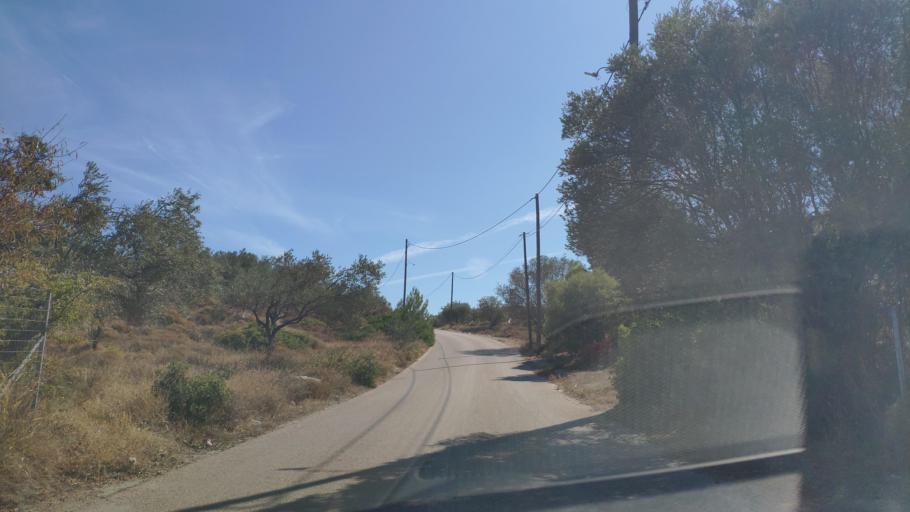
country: GR
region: Attica
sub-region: Nomarchia Anatolikis Attikis
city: Kouvaras
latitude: 37.8363
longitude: 23.9895
